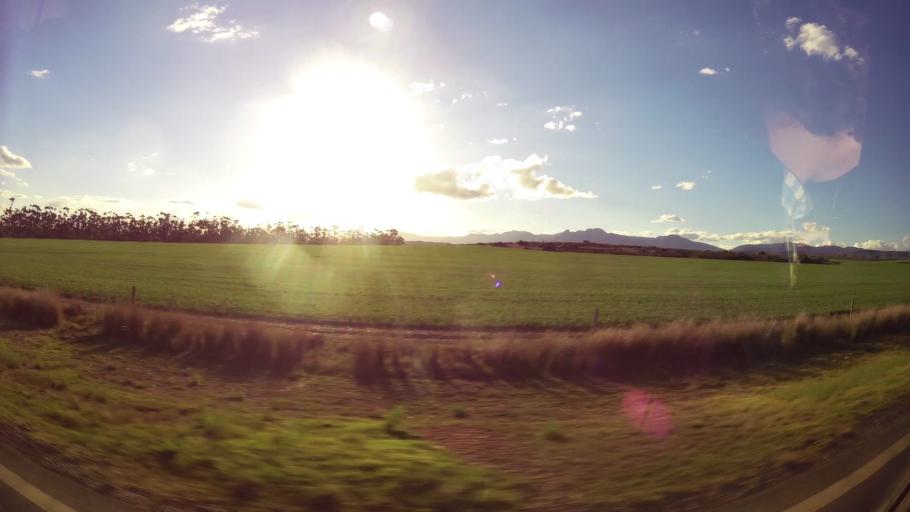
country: ZA
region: Western Cape
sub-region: Eden District Municipality
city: Riversdale
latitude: -34.0888
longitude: 20.9796
